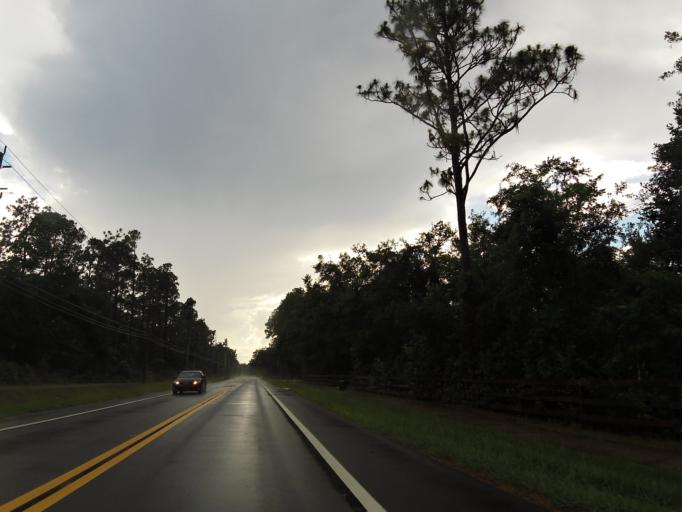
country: US
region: Florida
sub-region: Saint Johns County
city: Fruit Cove
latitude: 30.0632
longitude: -81.6552
